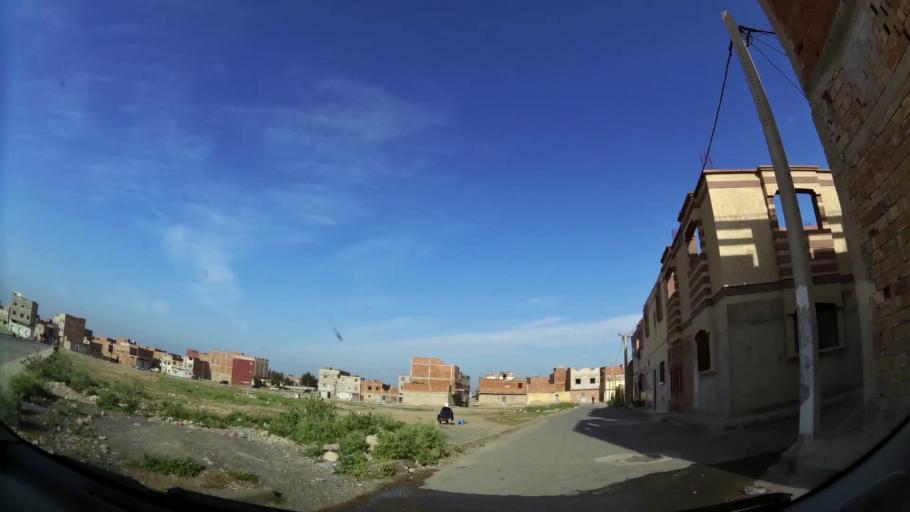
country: MA
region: Oriental
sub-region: Oujda-Angad
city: Oujda
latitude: 34.7168
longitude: -1.8987
